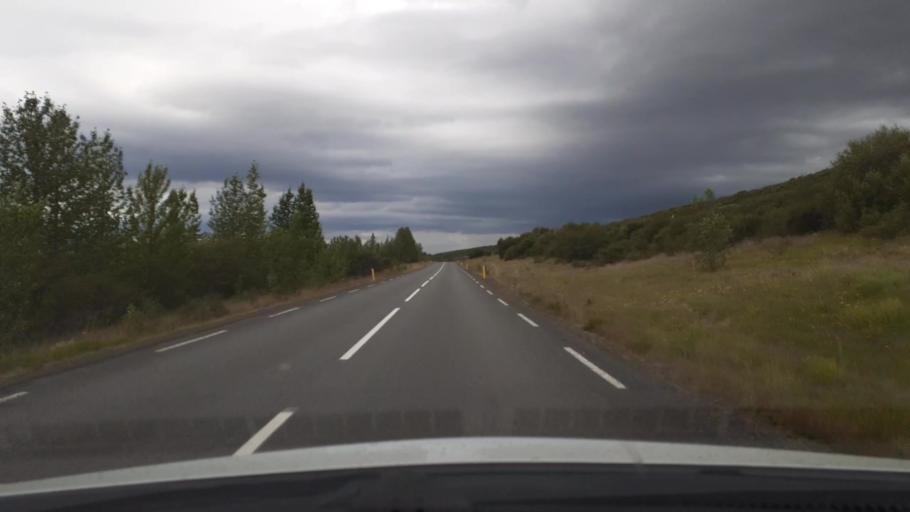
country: IS
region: West
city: Borgarnes
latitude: 64.5416
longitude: -21.5491
